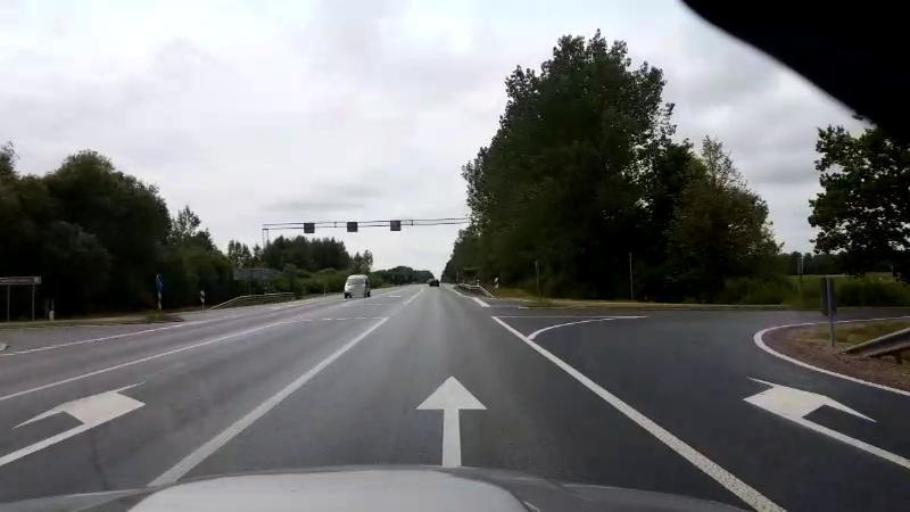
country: LV
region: Lecava
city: Iecava
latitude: 56.6794
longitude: 24.2375
